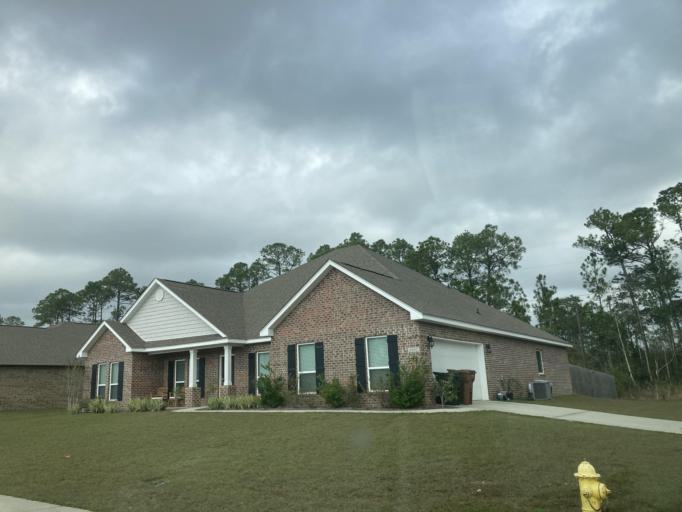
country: US
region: Mississippi
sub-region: Harrison County
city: D'Iberville
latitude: 30.4786
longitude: -88.9812
